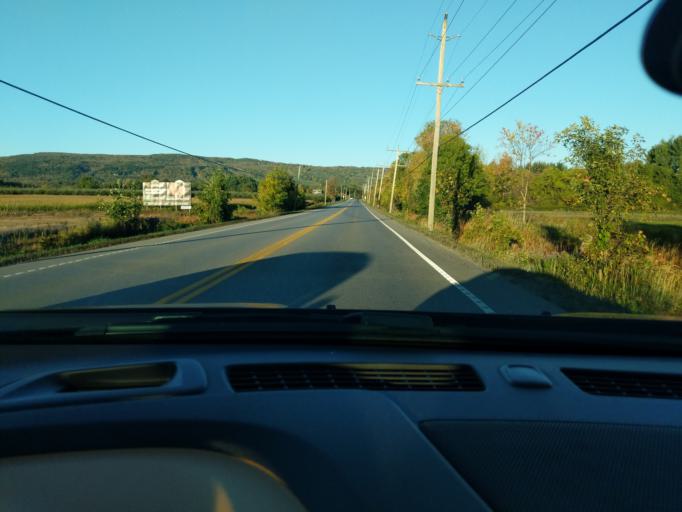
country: CA
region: Ontario
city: Collingwood
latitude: 44.4985
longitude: -80.2684
